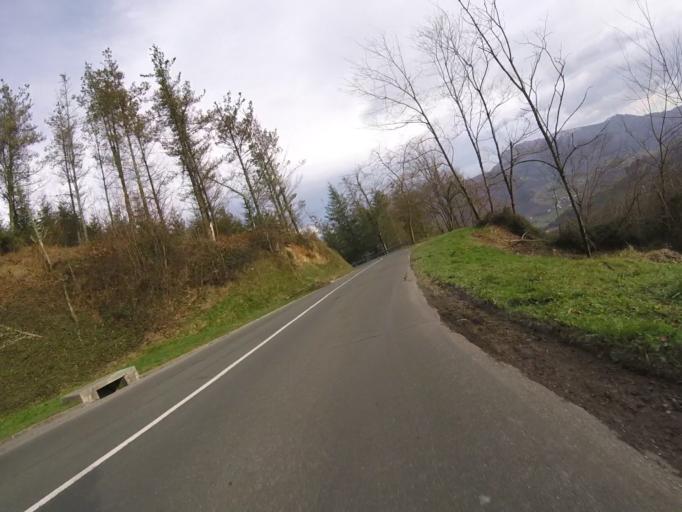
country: ES
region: Basque Country
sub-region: Provincia de Guipuzcoa
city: Beizama
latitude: 43.1604
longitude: -2.2074
